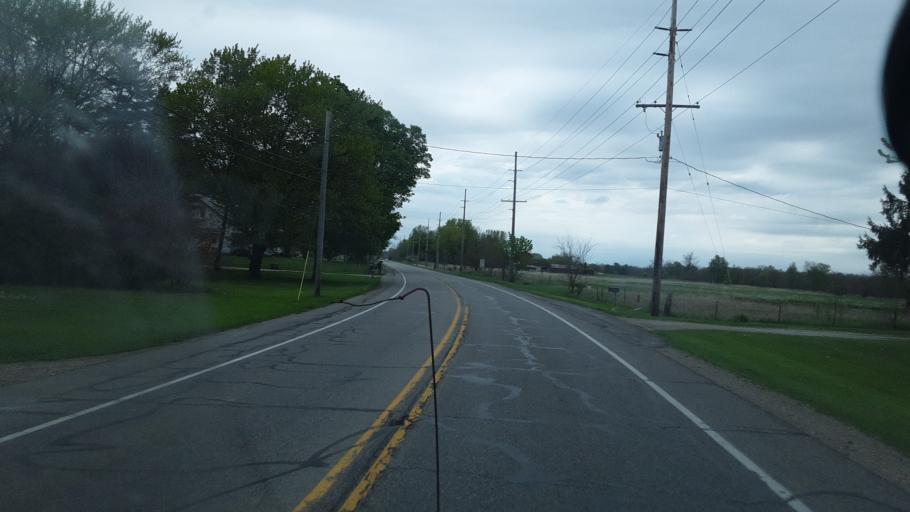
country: US
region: Indiana
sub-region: Elkhart County
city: Goshen
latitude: 41.6114
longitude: -85.8304
